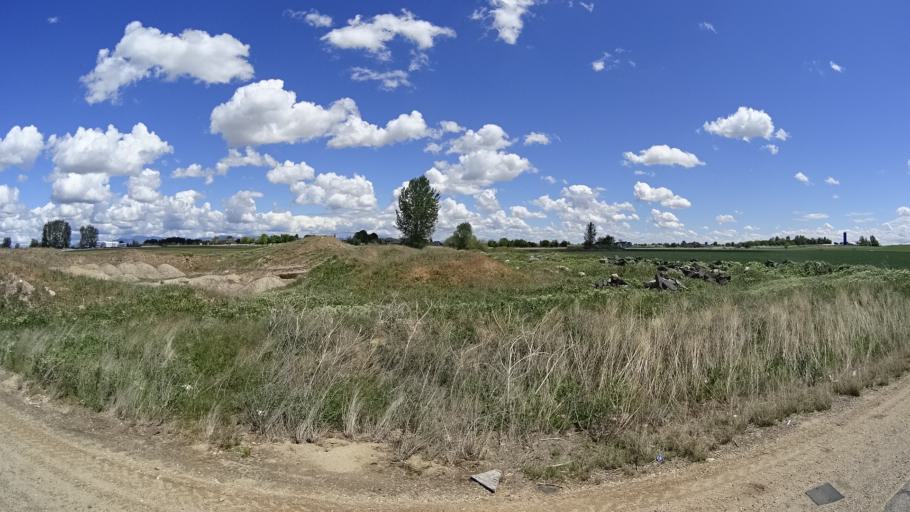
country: US
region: Idaho
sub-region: Ada County
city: Meridian
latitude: 43.5709
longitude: -116.4337
